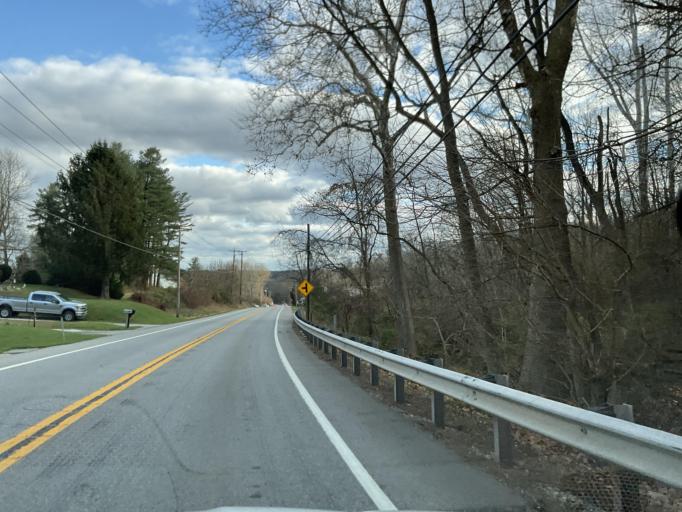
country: US
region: Pennsylvania
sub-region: Adams County
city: Mount Pleasant
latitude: 39.6779
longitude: -77.0374
